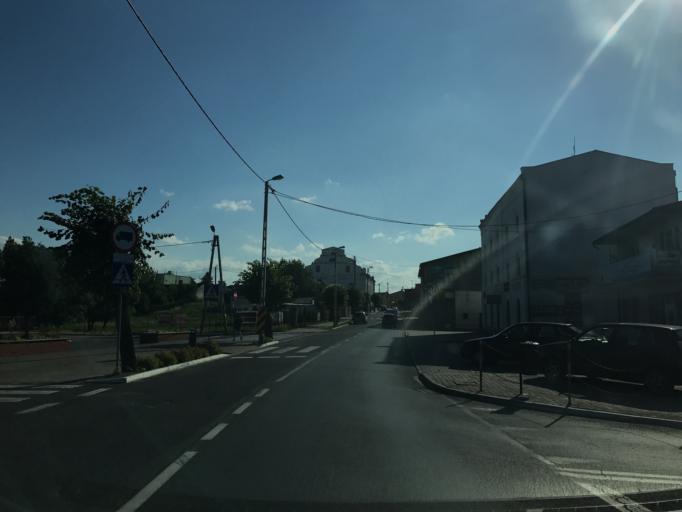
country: PL
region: Kujawsko-Pomorskie
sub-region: Powiat wloclawski
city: Lubraniec
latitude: 52.5425
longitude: 18.8343
